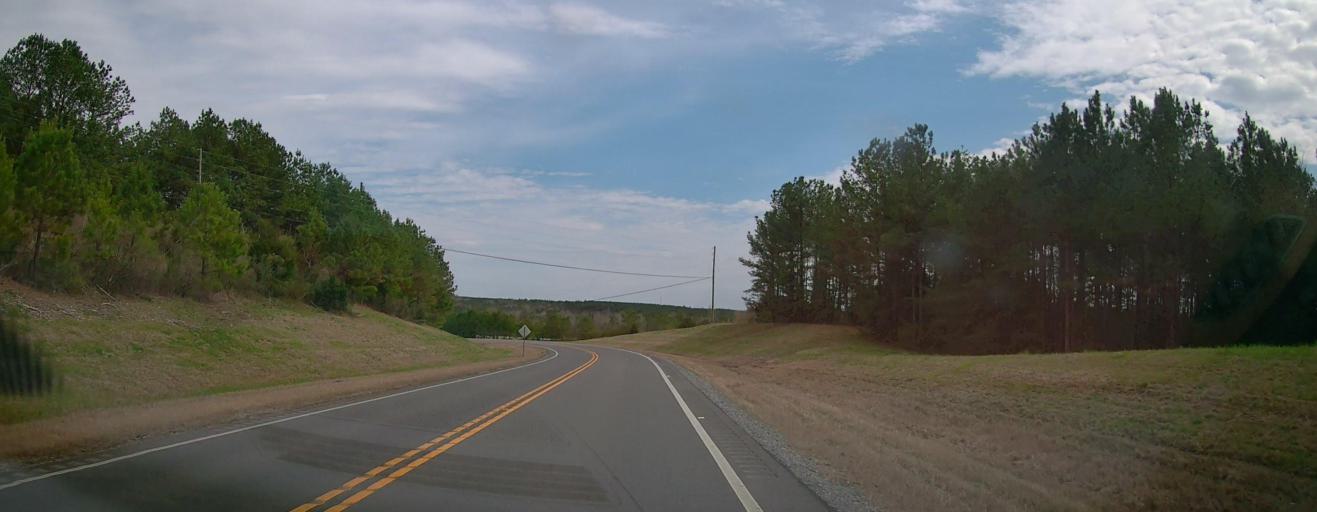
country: US
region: Alabama
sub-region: Walker County
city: Carbon Hill
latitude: 33.8659
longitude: -87.4101
